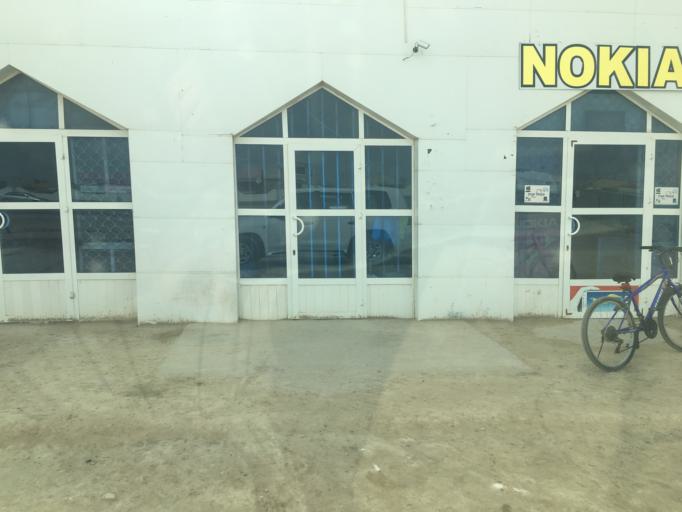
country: TM
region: Ahal
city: Tejen
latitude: 37.3686
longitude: 60.4980
